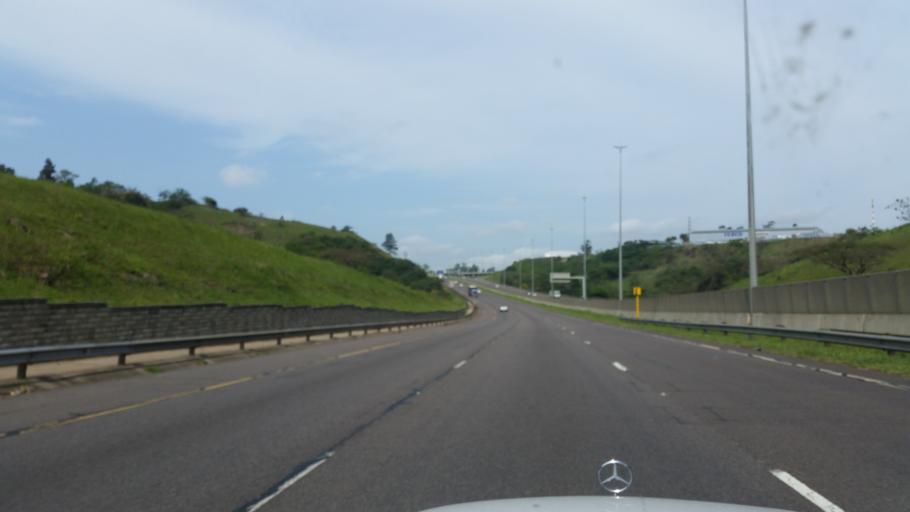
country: ZA
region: KwaZulu-Natal
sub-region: eThekwini Metropolitan Municipality
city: Berea
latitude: -29.8271
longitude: 30.8223
